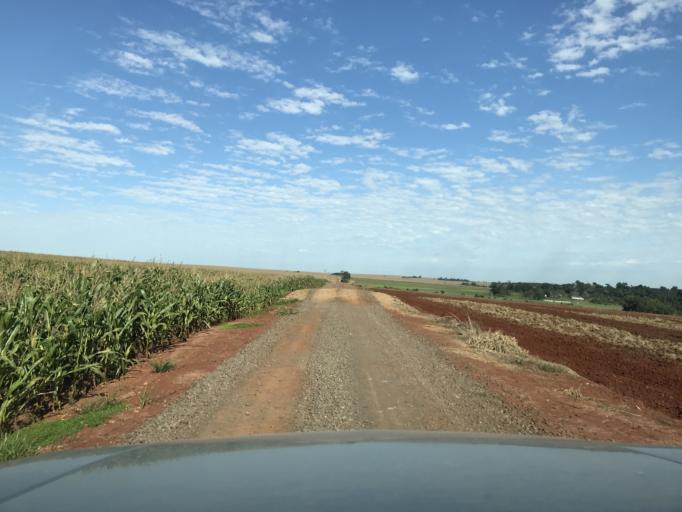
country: BR
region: Parana
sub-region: Palotina
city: Palotina
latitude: -24.1607
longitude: -53.7460
